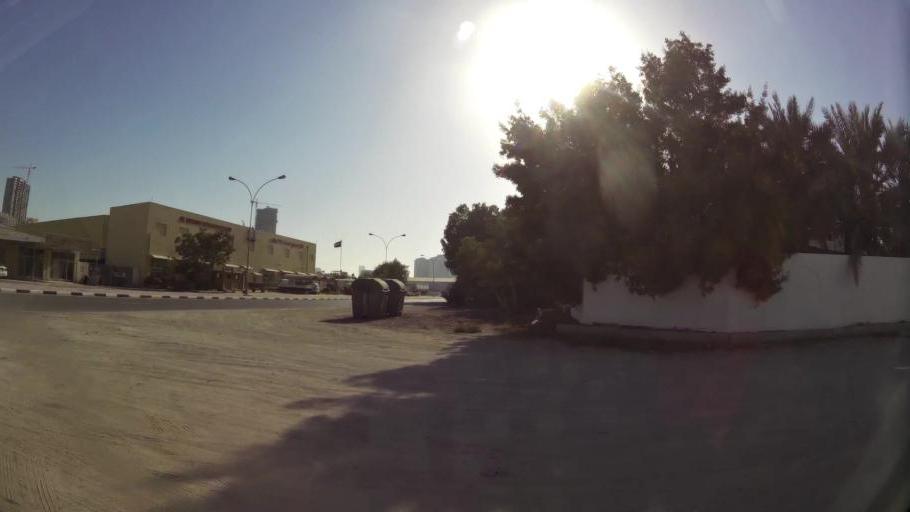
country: AE
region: Ajman
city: Ajman
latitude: 25.3996
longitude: 55.4611
